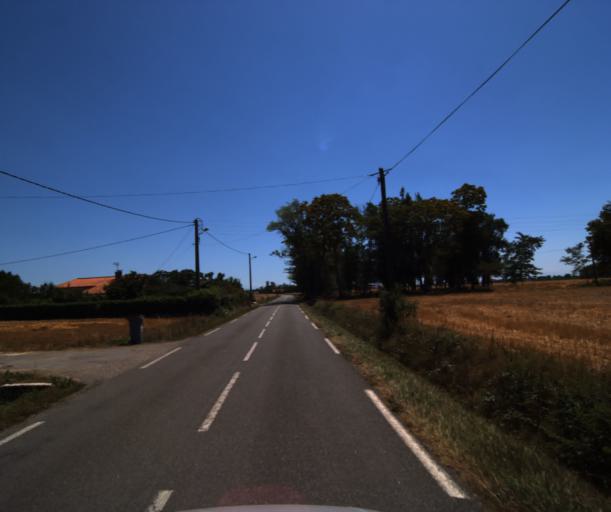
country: FR
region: Midi-Pyrenees
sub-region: Departement de la Haute-Garonne
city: Labastidette
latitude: 43.4529
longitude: 1.2922
